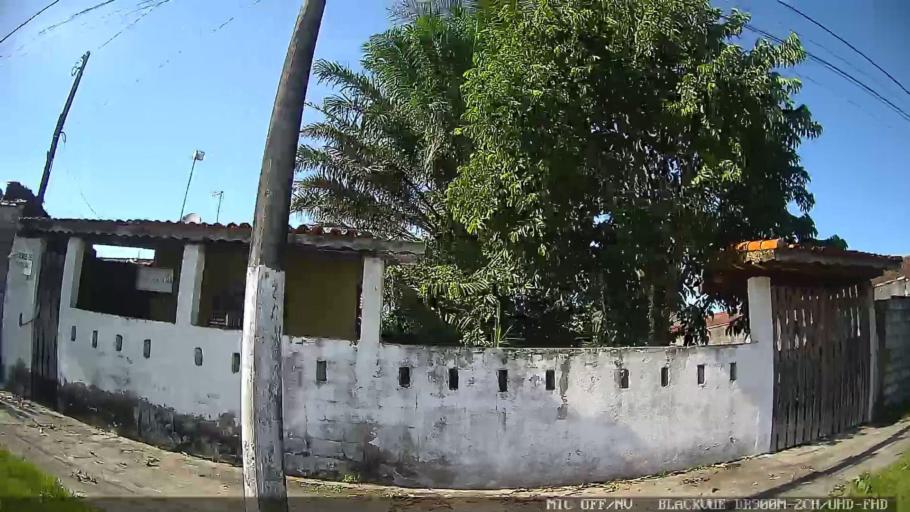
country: BR
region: Sao Paulo
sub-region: Itanhaem
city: Itanhaem
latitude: -24.2165
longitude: -46.8683
